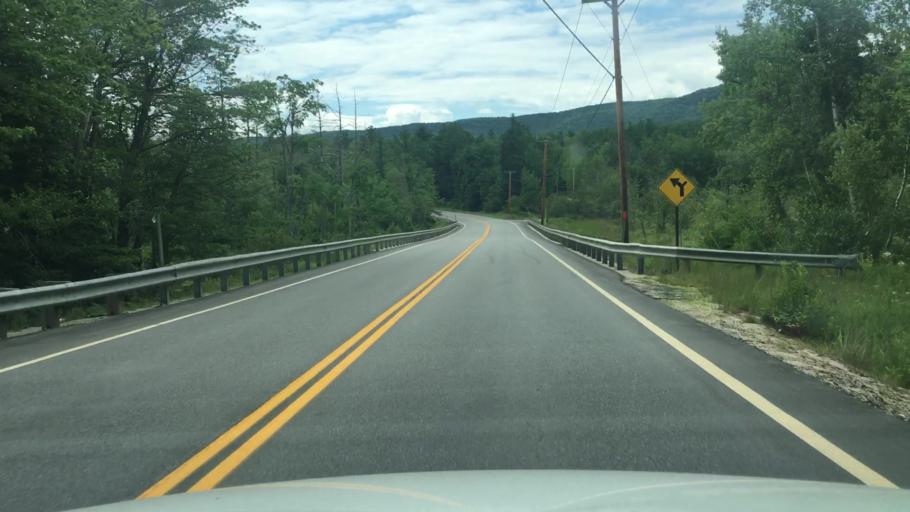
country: US
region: Maine
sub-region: Oxford County
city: West Paris
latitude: 44.3679
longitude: -70.4955
